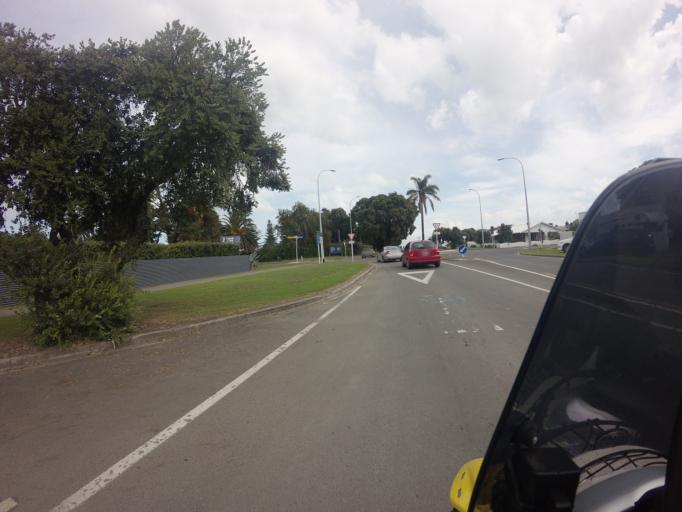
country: NZ
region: Gisborne
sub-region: Gisborne District
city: Gisborne
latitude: -38.6694
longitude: 178.0184
